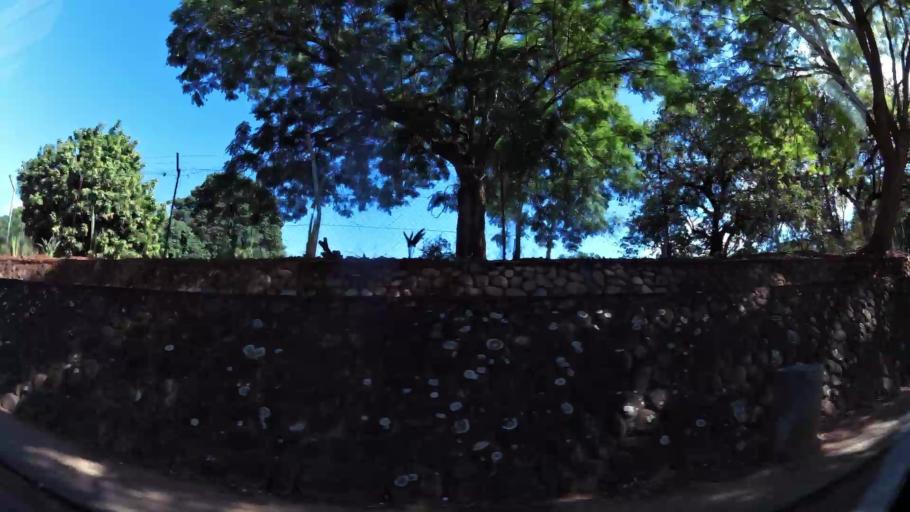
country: ZA
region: Limpopo
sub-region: Mopani District Municipality
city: Tzaneen
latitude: -23.8205
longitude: 30.1585
